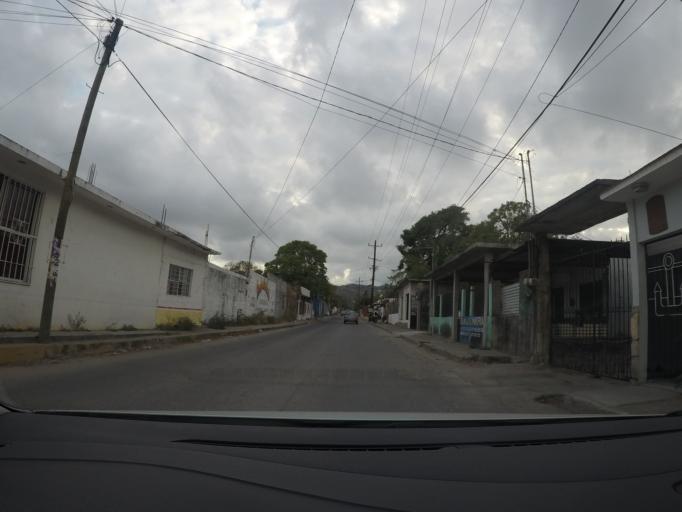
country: MX
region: Oaxaca
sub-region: Salina Cruz
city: Salina Cruz
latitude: 16.2048
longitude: -95.1979
